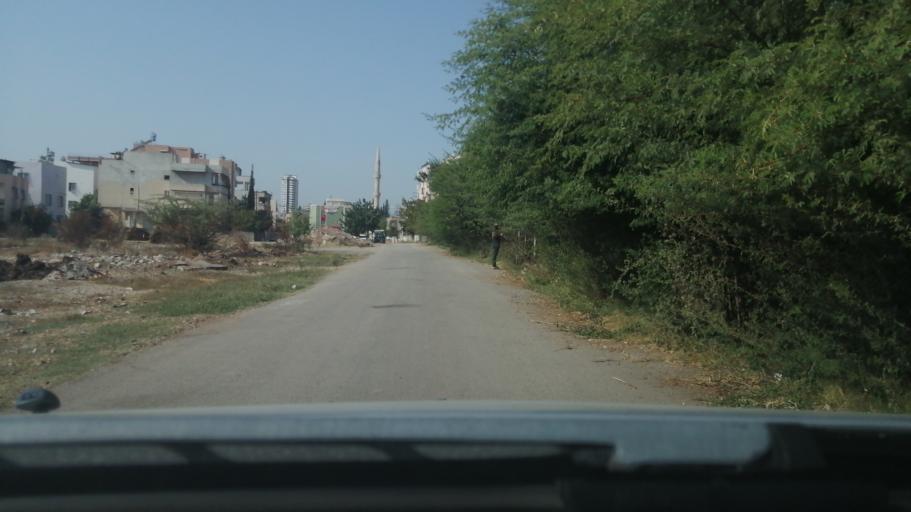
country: TR
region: Adana
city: Seyhan
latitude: 37.0179
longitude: 35.2785
